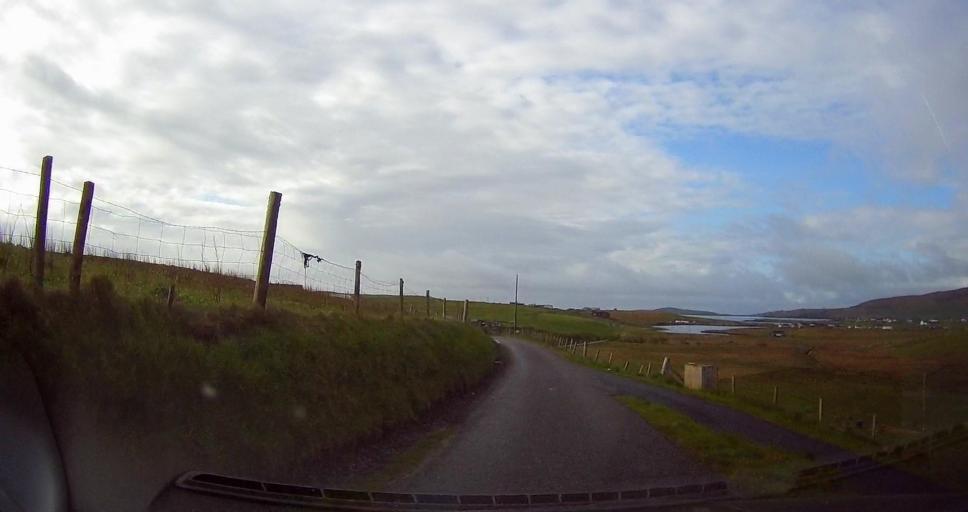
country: GB
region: Scotland
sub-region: Shetland Islands
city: Sandwick
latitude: 60.0523
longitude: -1.2076
